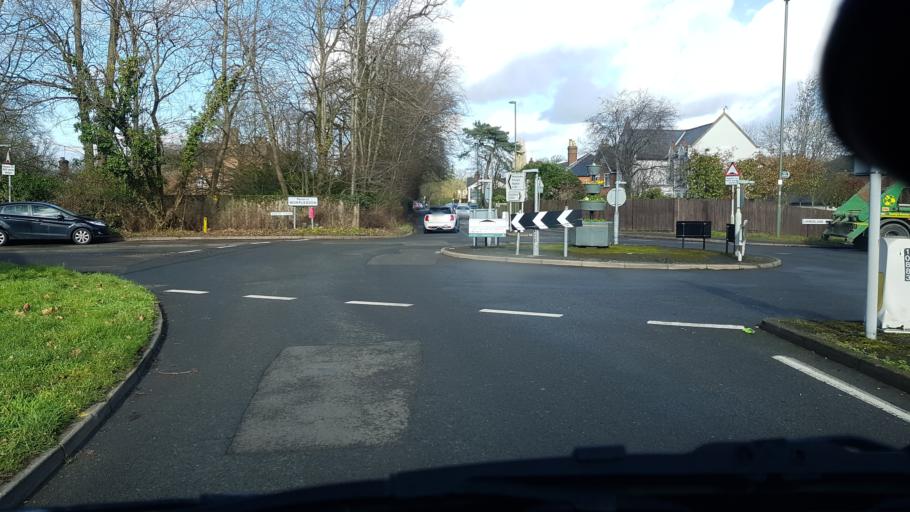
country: GB
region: England
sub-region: Surrey
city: Guildford
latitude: 51.2627
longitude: -0.5965
